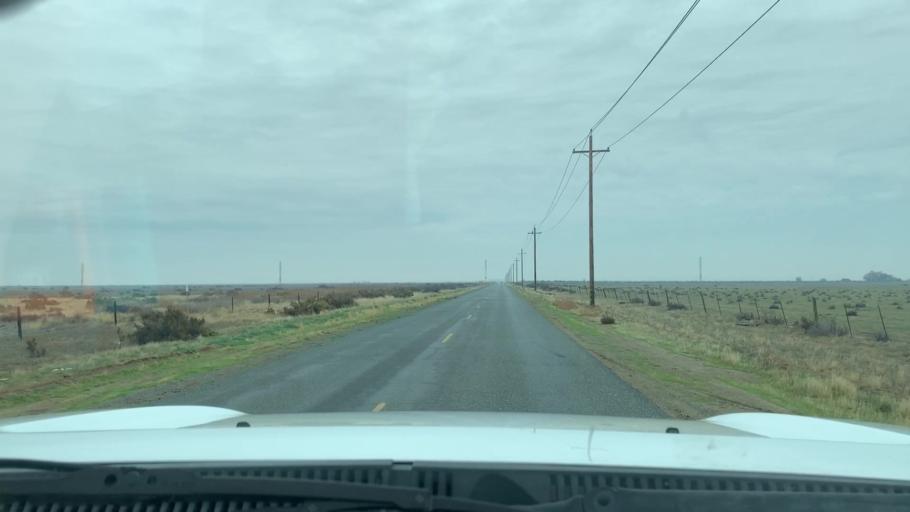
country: US
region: California
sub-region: Tulare County
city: Alpaugh
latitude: 35.7610
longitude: -119.4628
